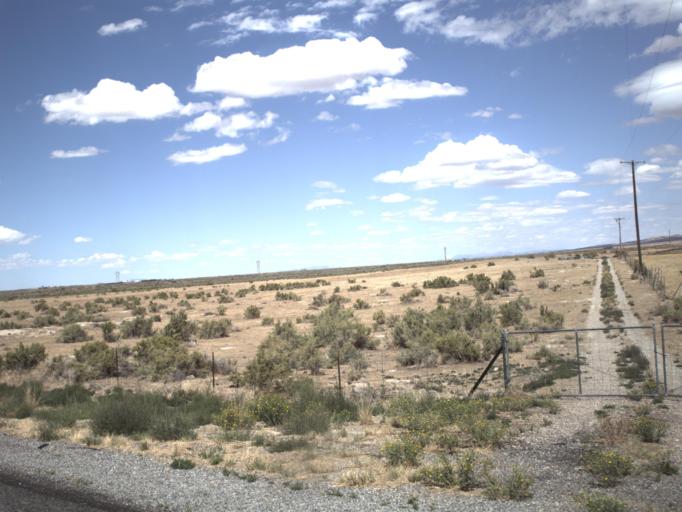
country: US
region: Utah
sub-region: Millard County
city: Fillmore
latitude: 39.1426
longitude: -112.3797
